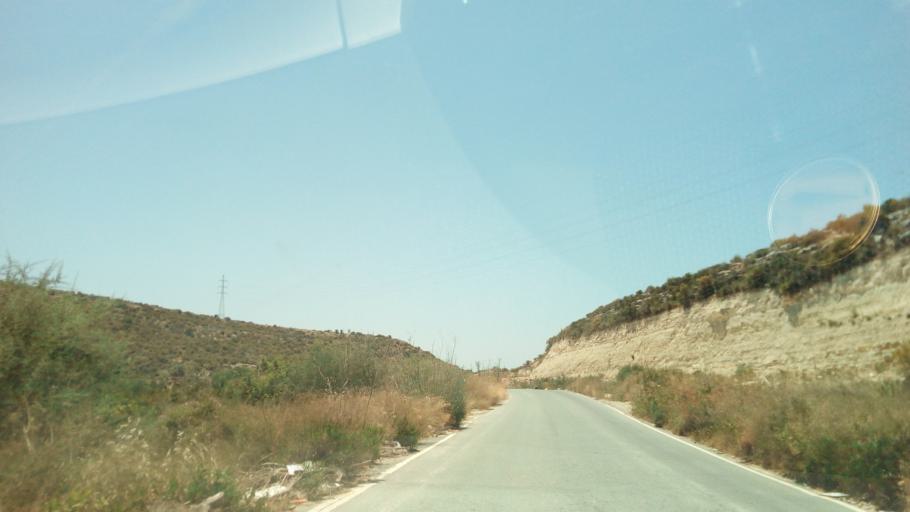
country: CY
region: Limassol
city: Ypsonas
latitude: 34.7219
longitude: 32.9528
